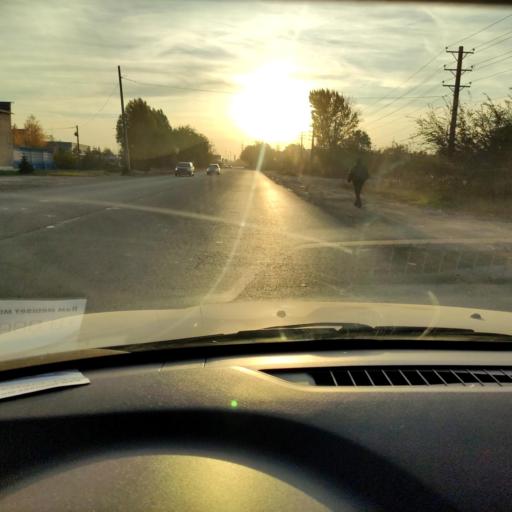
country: RU
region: Samara
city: Tol'yatti
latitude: 53.5303
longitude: 49.4662
